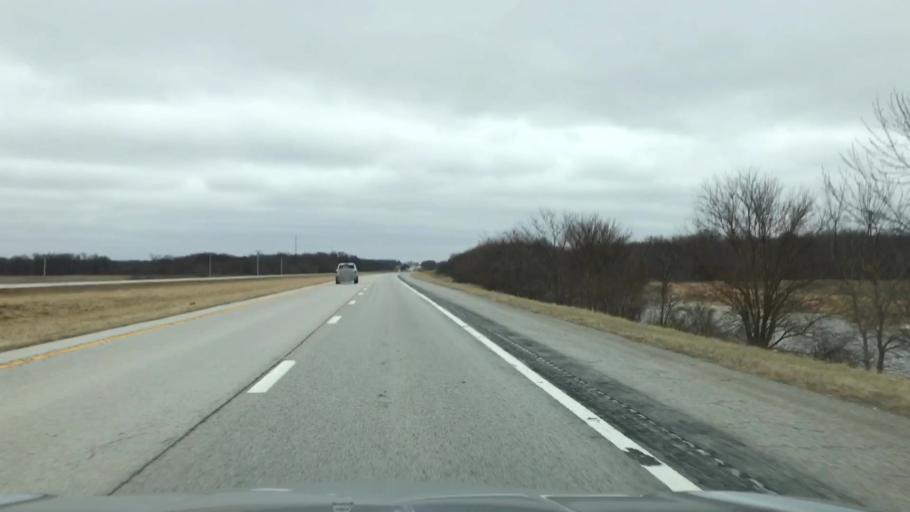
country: US
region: Missouri
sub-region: Linn County
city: Linneus
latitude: 39.7774
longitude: -93.3339
